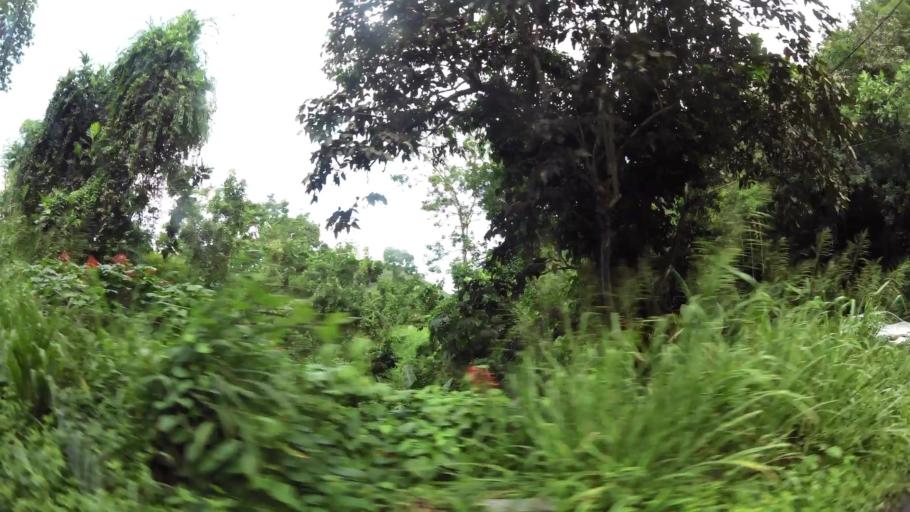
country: MQ
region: Martinique
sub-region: Martinique
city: Les Trois-Ilets
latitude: 14.5191
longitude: -61.0738
